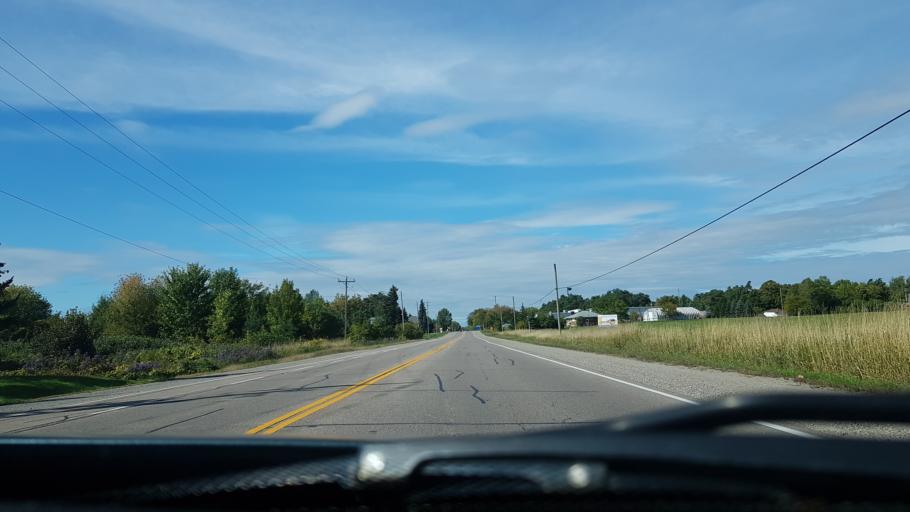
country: CA
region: Ontario
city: Orillia
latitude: 44.5995
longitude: -79.3386
